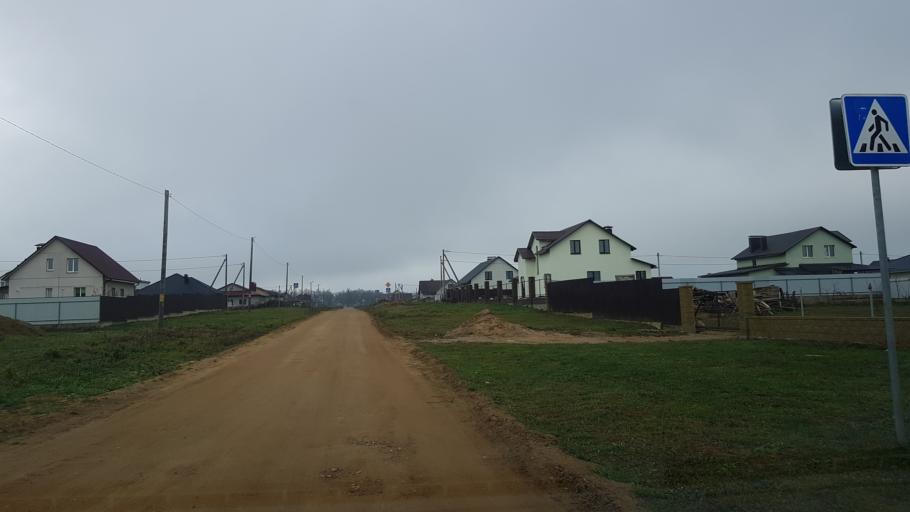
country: BY
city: Fanipol
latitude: 53.7313
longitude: 27.3226
